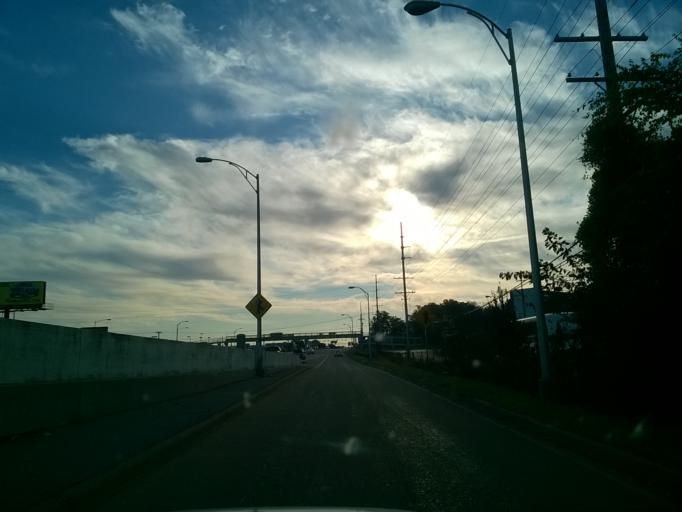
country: US
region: Indiana
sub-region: Vanderburgh County
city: Melody Hill
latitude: 37.9765
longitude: -87.4889
